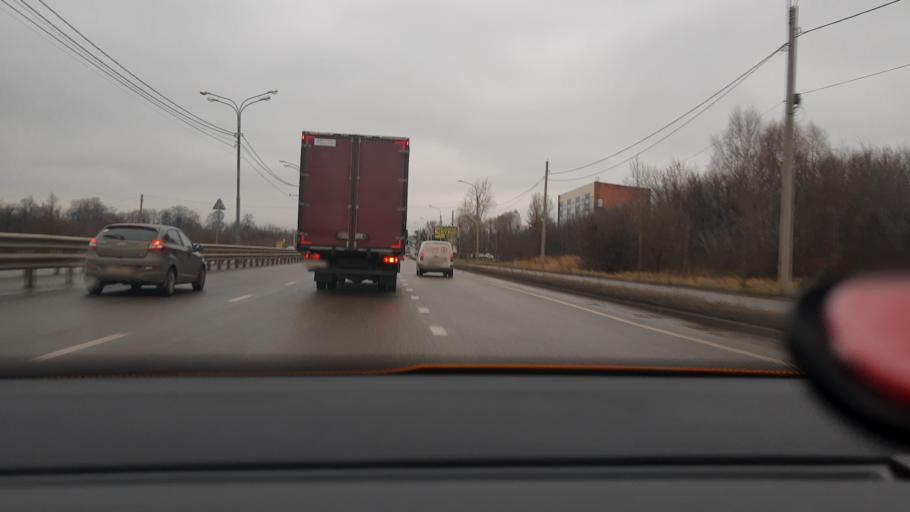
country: RU
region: Moskovskaya
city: Dolgoprudnyy
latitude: 55.9198
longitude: 37.4940
